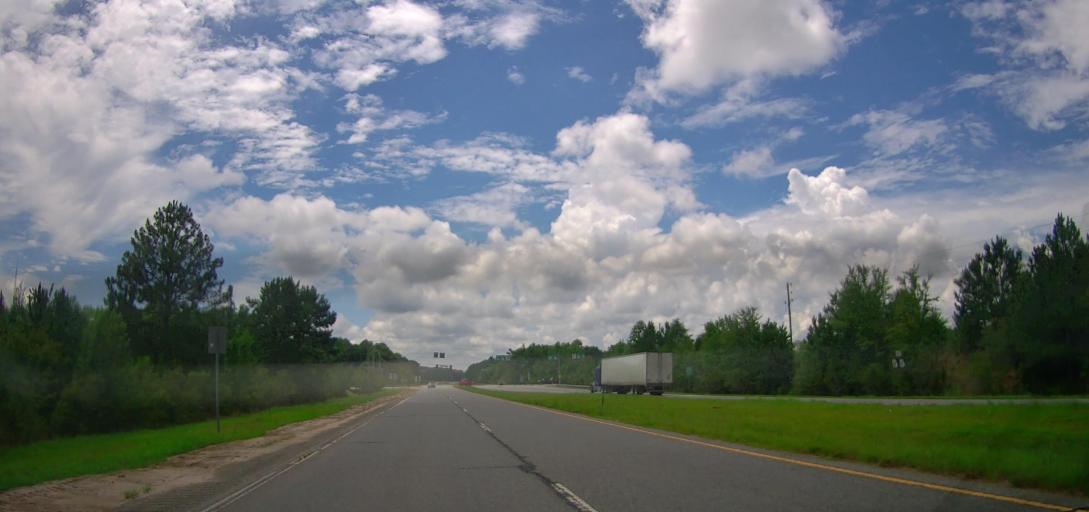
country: US
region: Georgia
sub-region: Dodge County
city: Eastman
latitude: 32.1774
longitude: -83.1794
